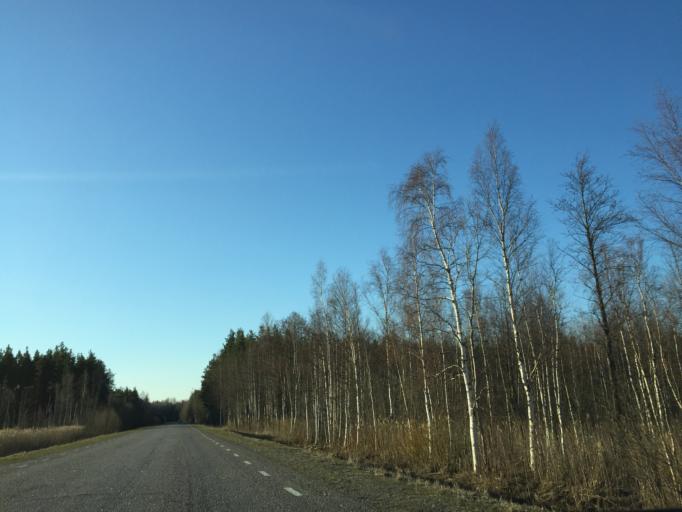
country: EE
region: Ida-Virumaa
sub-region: Toila vald
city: Voka
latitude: 59.1183
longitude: 27.6317
